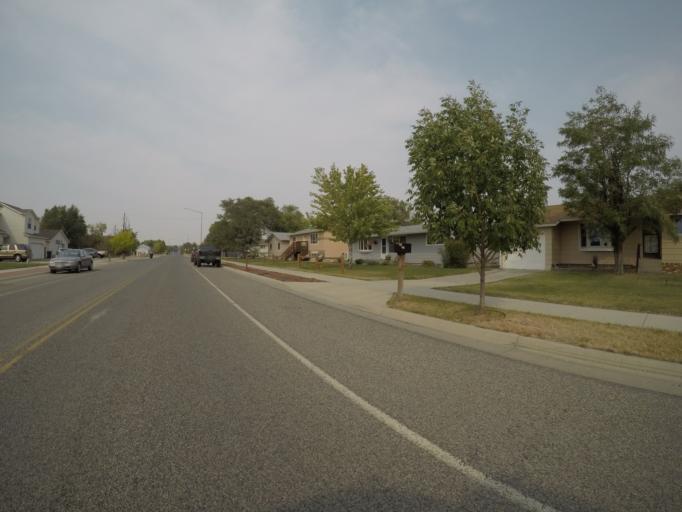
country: US
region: Montana
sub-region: Yellowstone County
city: Laurel
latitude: 45.6696
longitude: -108.7820
